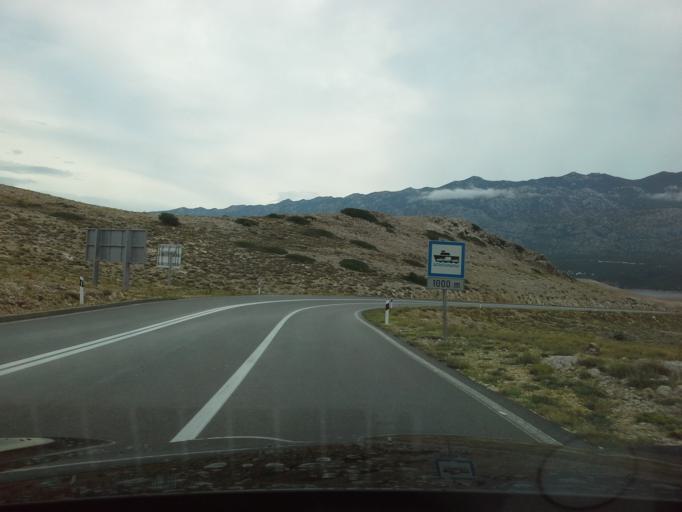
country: HR
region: Primorsko-Goranska
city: Banjol
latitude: 44.7046
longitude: 14.8487
